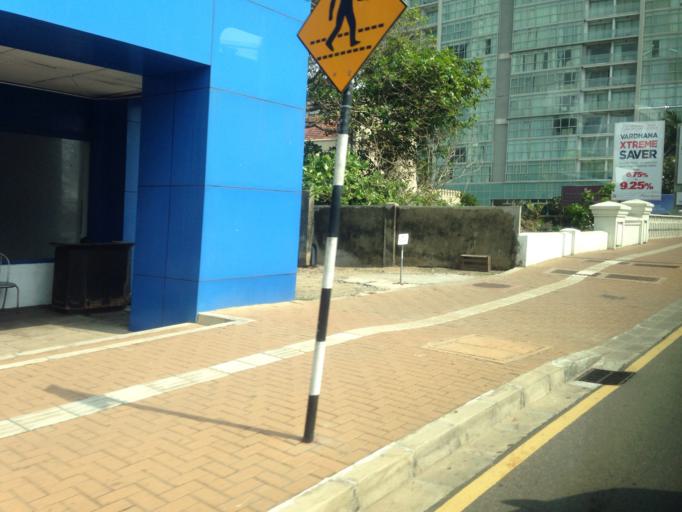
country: LK
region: Western
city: Colombo
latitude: 6.9194
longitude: 79.8471
